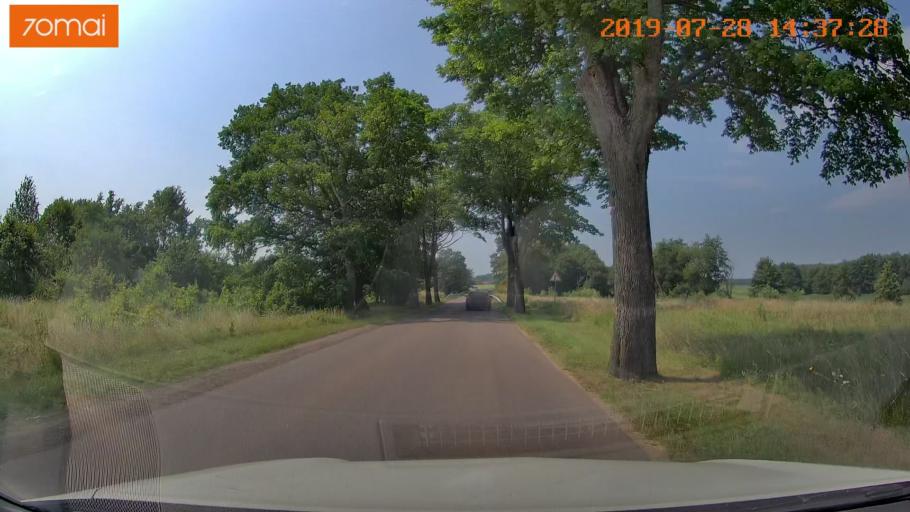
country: RU
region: Kaliningrad
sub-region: Gorod Kaliningrad
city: Yantarnyy
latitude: 54.8407
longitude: 19.9975
